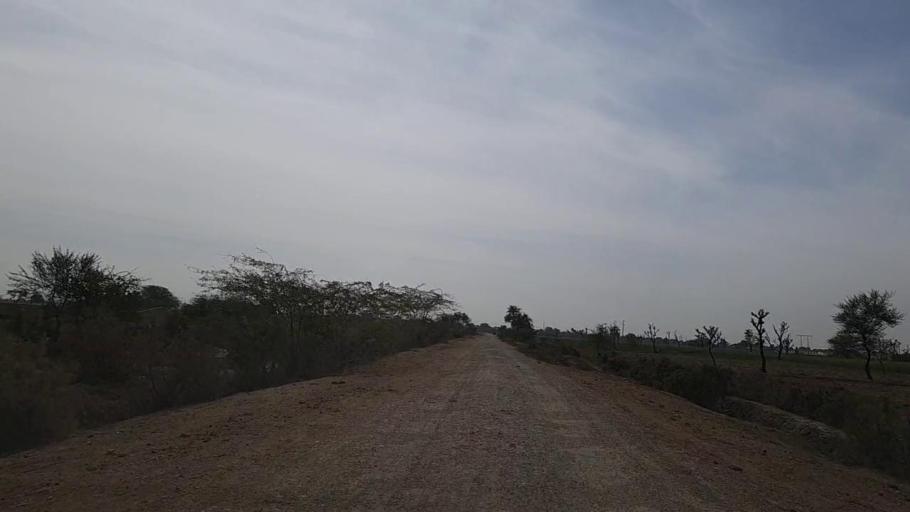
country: PK
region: Sindh
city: Samaro
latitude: 25.2988
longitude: 69.4189
